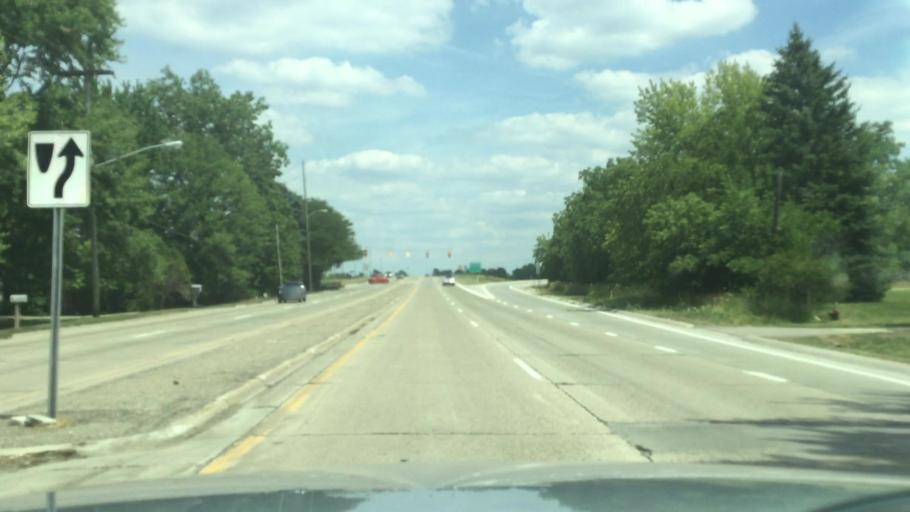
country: US
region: Michigan
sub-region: Genesee County
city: Grand Blanc
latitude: 42.9441
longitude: -83.6863
